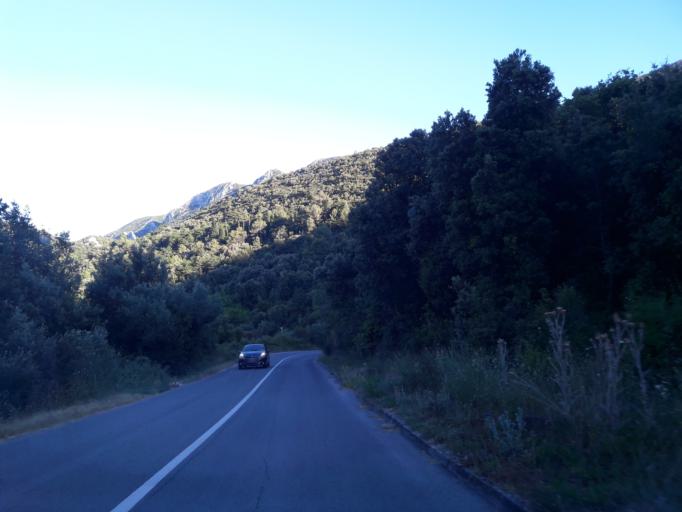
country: HR
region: Dubrovacko-Neretvanska
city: Orebic
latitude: 42.9958
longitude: 17.2638
